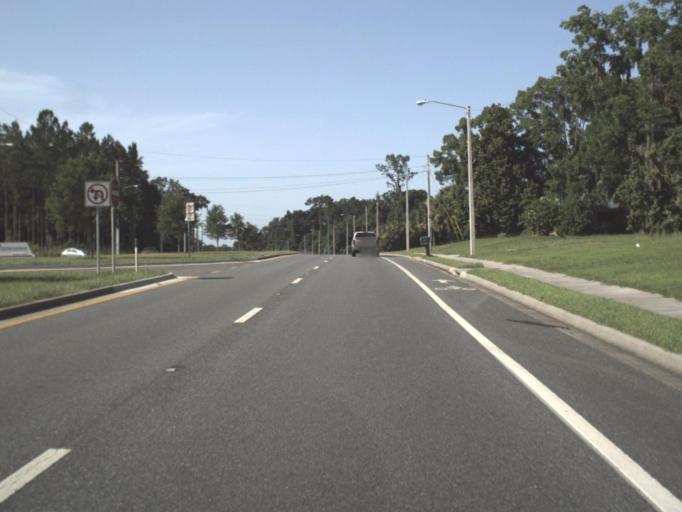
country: US
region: Florida
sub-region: Columbia County
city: Lake City
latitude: 30.1473
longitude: -82.6500
